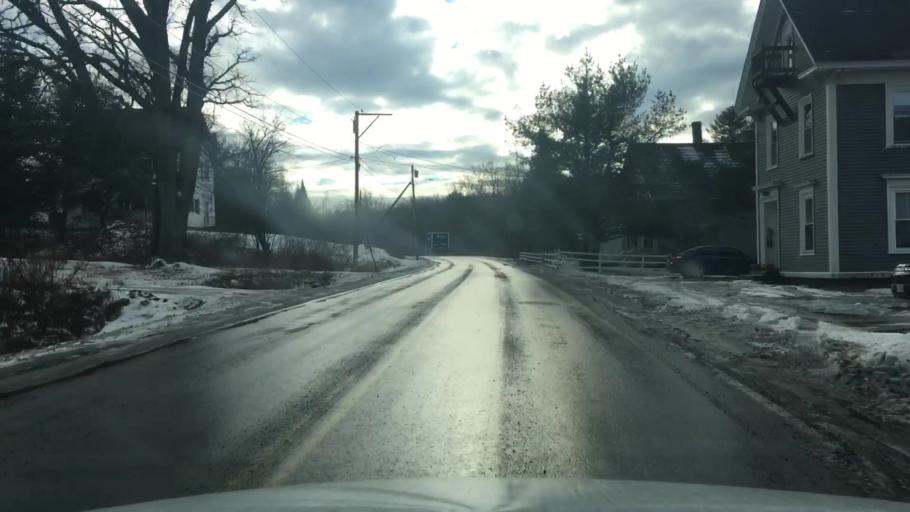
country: US
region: Maine
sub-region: Penobscot County
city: Brewer
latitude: 44.7627
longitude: -68.7758
